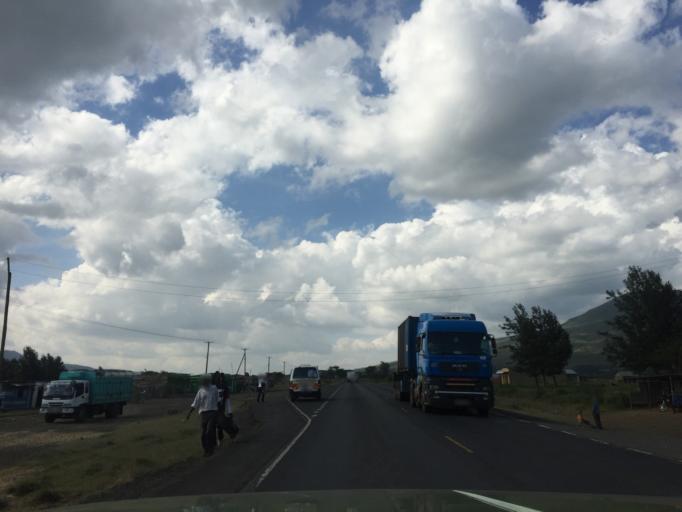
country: KE
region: Nakuru
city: Kijabe
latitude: -0.9534
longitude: 36.5519
